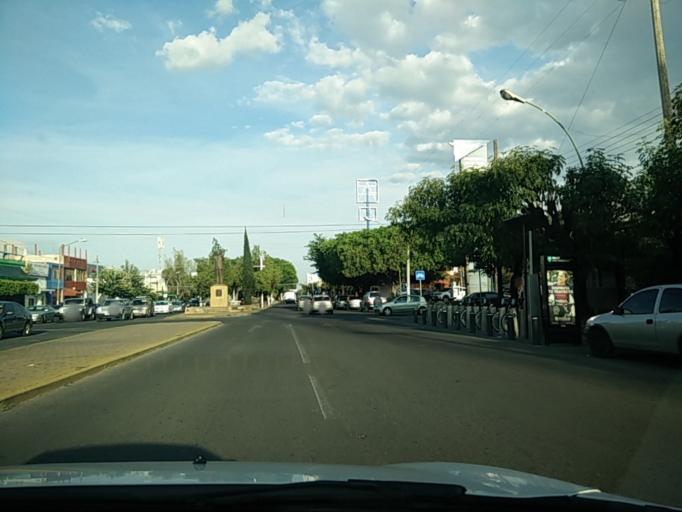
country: MX
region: Jalisco
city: Guadalajara
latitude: 20.6792
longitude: -103.3731
